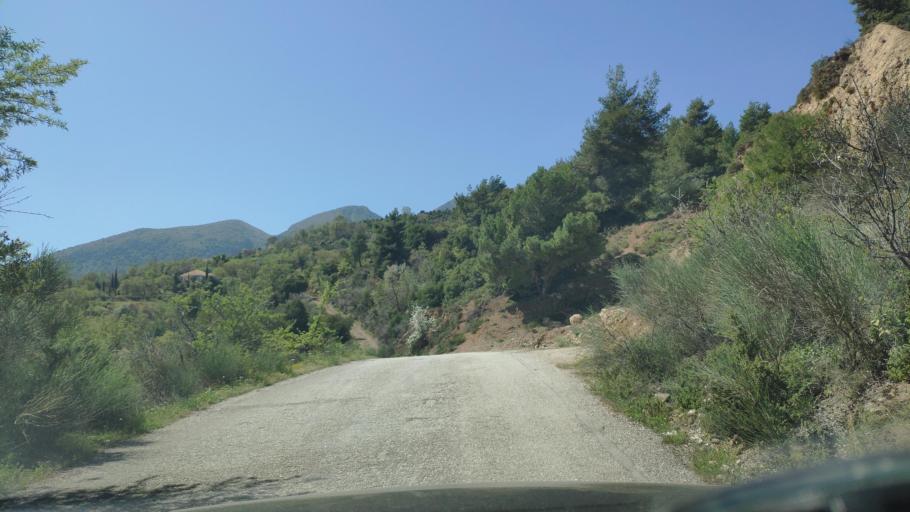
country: GR
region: West Greece
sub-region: Nomos Achaias
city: Akrata
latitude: 38.0891
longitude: 22.3234
